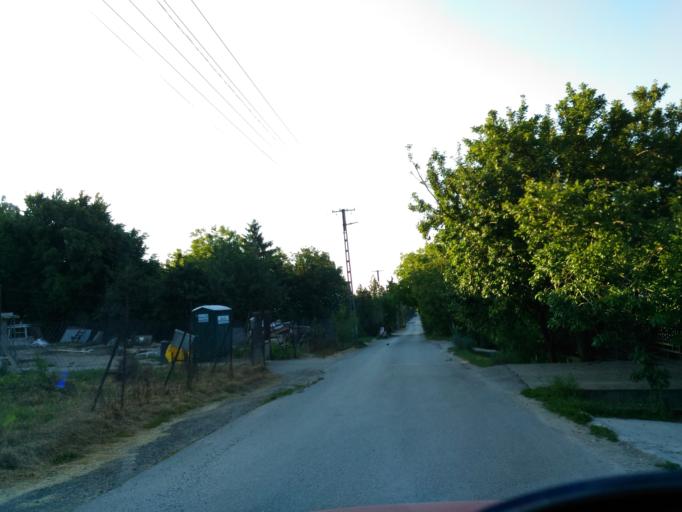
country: HU
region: Pest
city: Diosd
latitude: 47.3970
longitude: 18.9369
